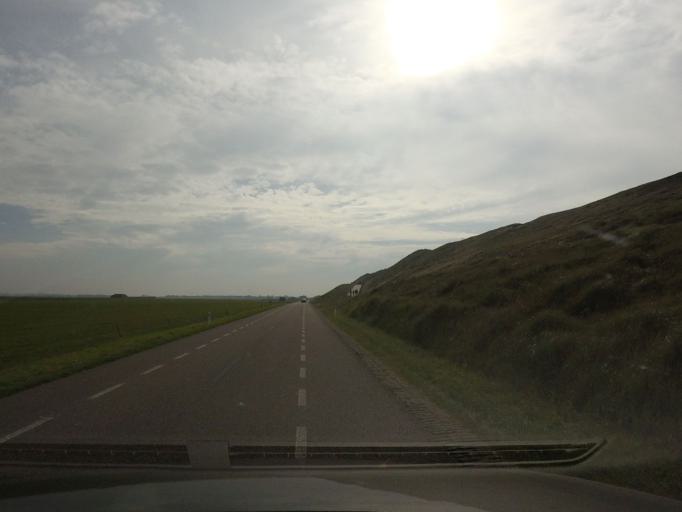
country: NL
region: North Holland
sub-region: Gemeente Den Helder
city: Den Helder
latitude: 52.8799
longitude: 4.7153
